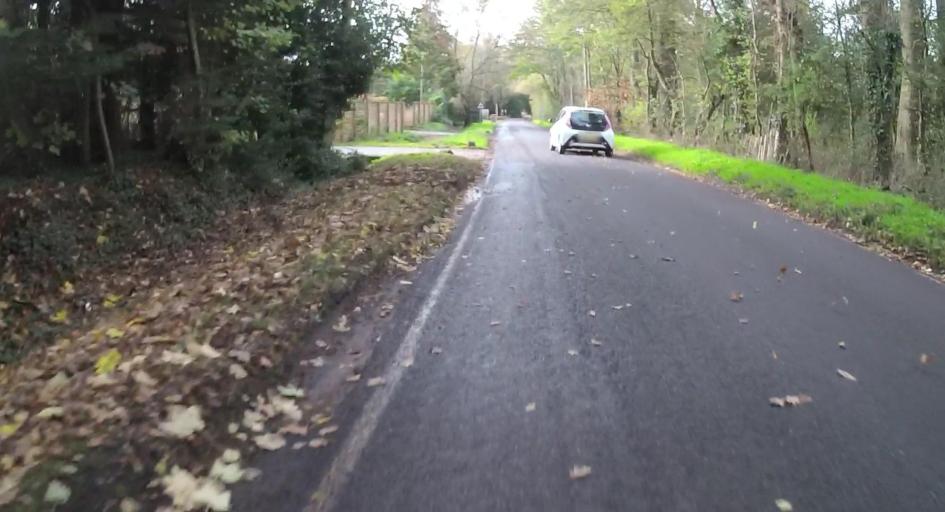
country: GB
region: England
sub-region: West Berkshire
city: Arborfield
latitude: 51.4032
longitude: -0.9163
